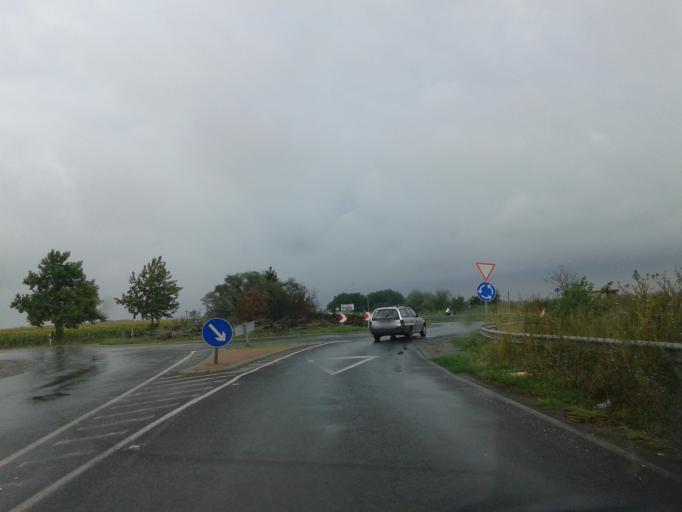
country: HU
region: Csongrad
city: Szeged
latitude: 46.2520
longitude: 20.0812
